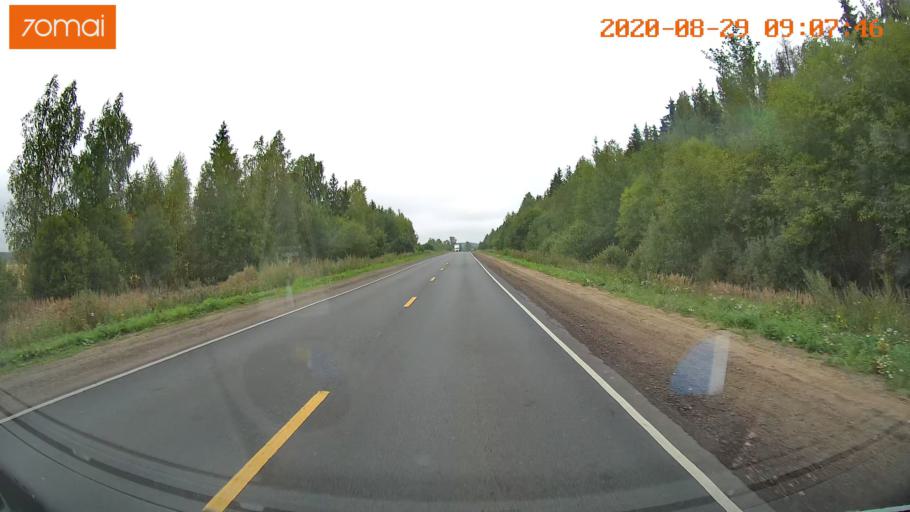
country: RU
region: Ivanovo
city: Kineshma
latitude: 57.3857
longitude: 42.0374
